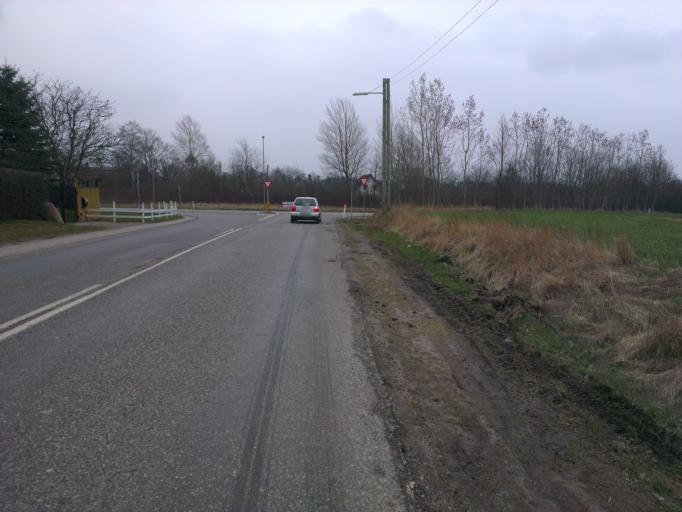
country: DK
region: Capital Region
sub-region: Frederikssund Kommune
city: Slangerup
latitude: 55.8305
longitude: 12.1625
